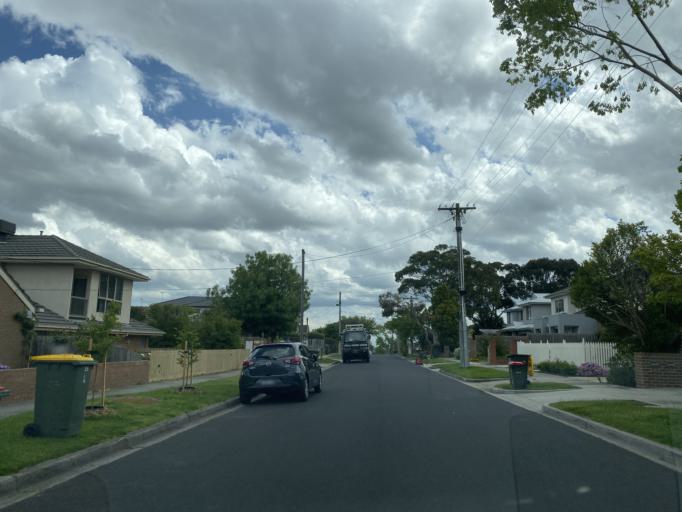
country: AU
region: Victoria
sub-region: Whitehorse
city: Burwood
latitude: -37.8531
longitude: 145.1311
